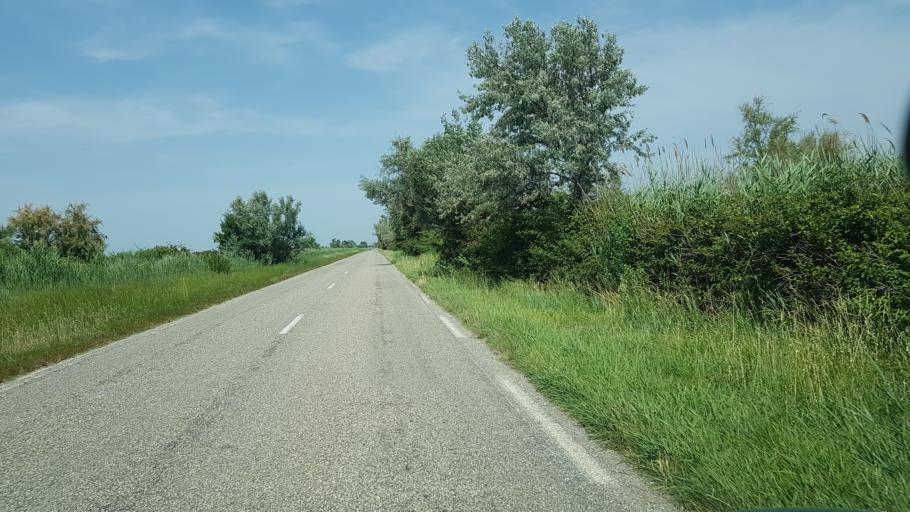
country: FR
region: Languedoc-Roussillon
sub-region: Departement du Gard
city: Saint-Gilles
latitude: 43.5743
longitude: 4.5252
